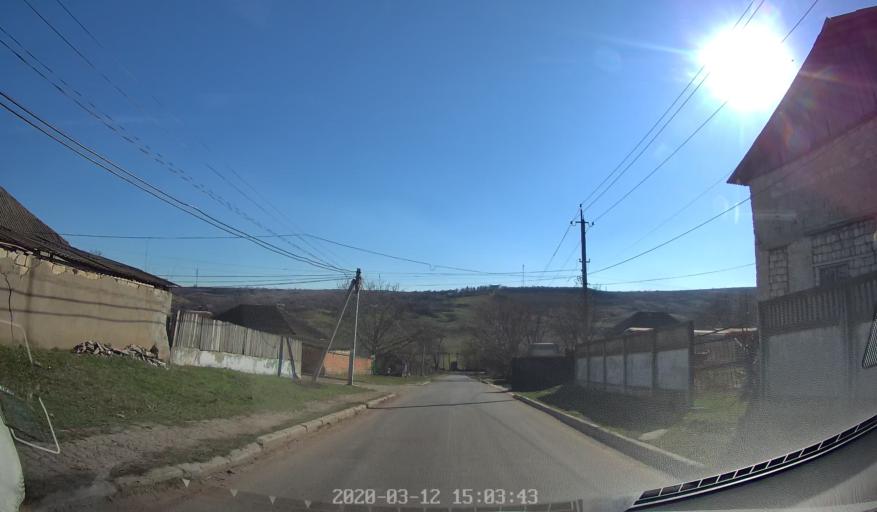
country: MD
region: Telenesti
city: Cocieri
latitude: 47.2224
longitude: 29.0195
